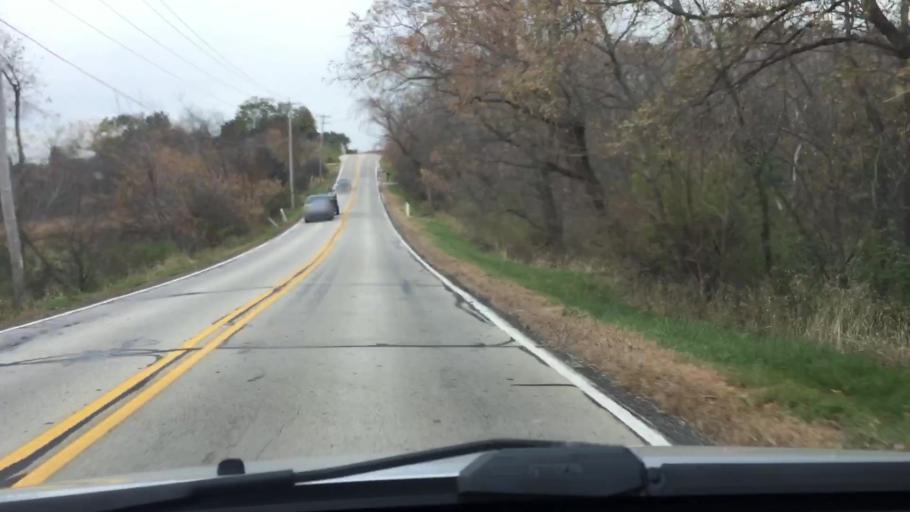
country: US
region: Wisconsin
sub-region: Waukesha County
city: New Berlin
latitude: 42.9445
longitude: -88.1019
